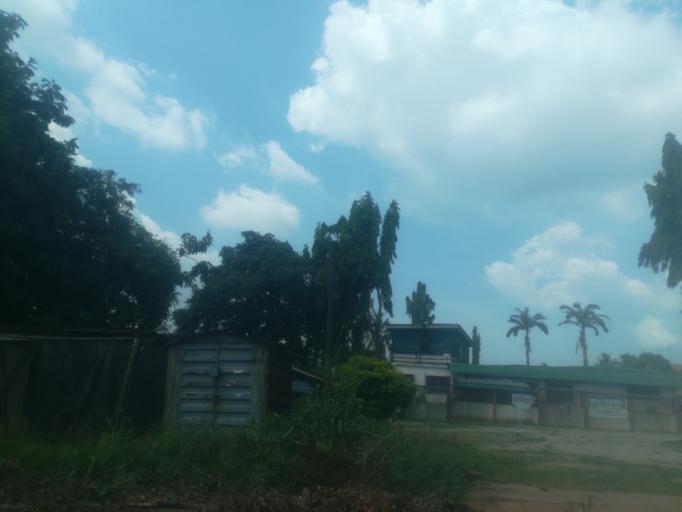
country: NG
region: Ogun
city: Abeokuta
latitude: 7.1749
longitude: 3.3813
